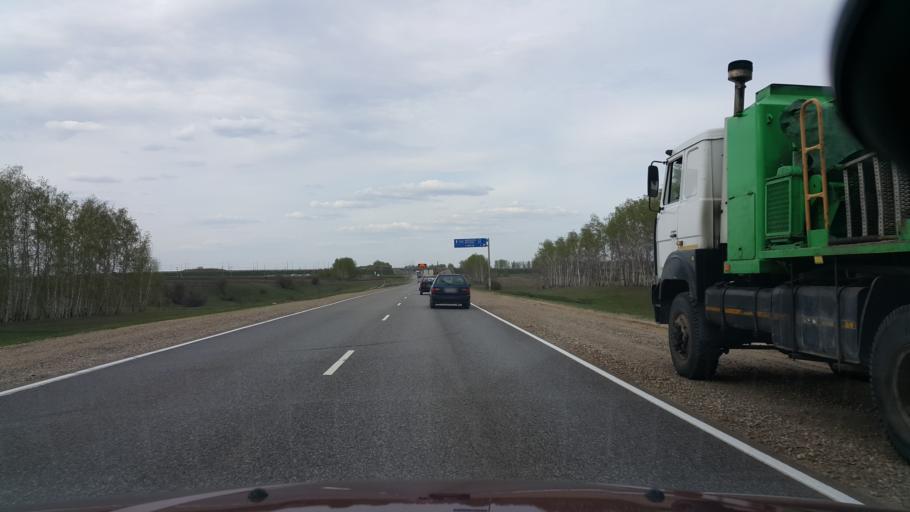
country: RU
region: Tambov
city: Pokrovo-Prigorodnoye
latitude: 52.6537
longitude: 41.3404
